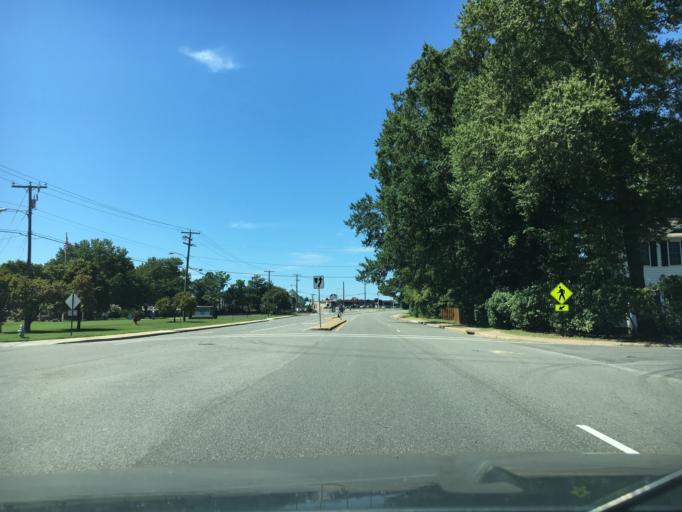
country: US
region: Virginia
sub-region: Henrico County
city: Tuckahoe
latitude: 37.6024
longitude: -77.5566
